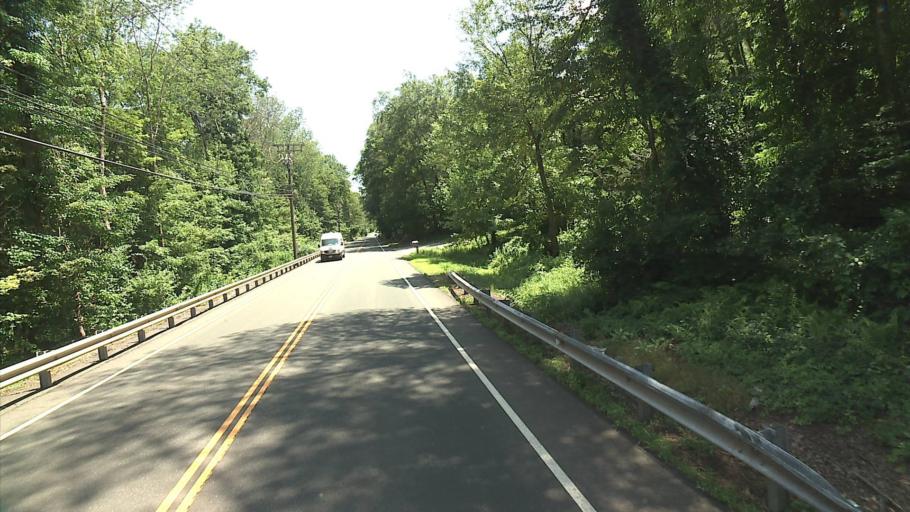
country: US
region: Connecticut
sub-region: Middlesex County
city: East Haddam
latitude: 41.4334
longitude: -72.4561
